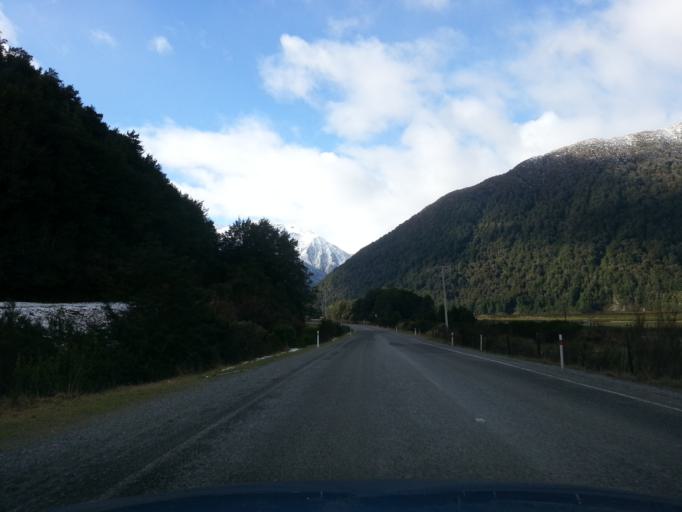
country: NZ
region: West Coast
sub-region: Grey District
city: Greymouth
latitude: -42.7781
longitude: 171.6156
